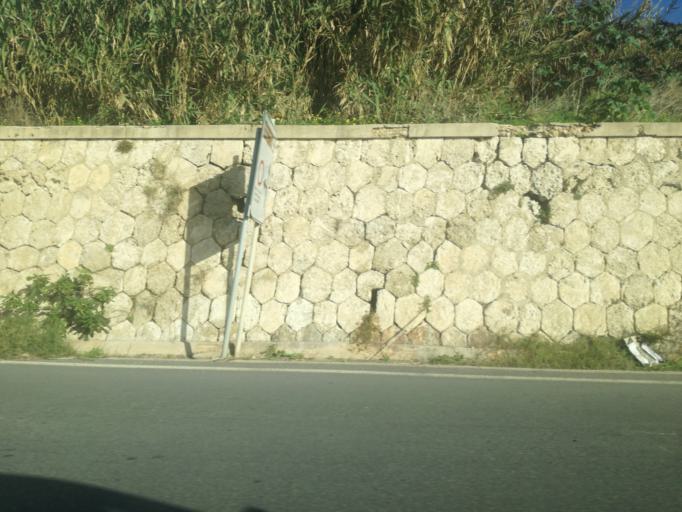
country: IT
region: Sicily
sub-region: Provincia di Caltanissetta
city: Gela
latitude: 37.0671
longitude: 14.2360
